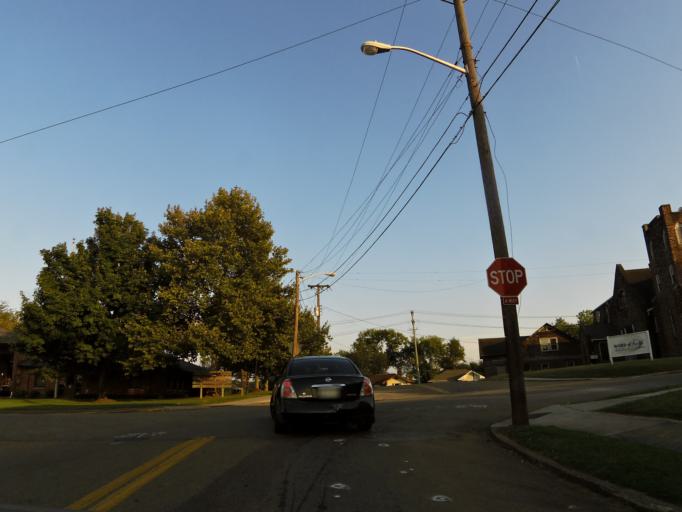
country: US
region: Tennessee
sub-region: Knox County
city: Knoxville
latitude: 35.9810
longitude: -83.8996
